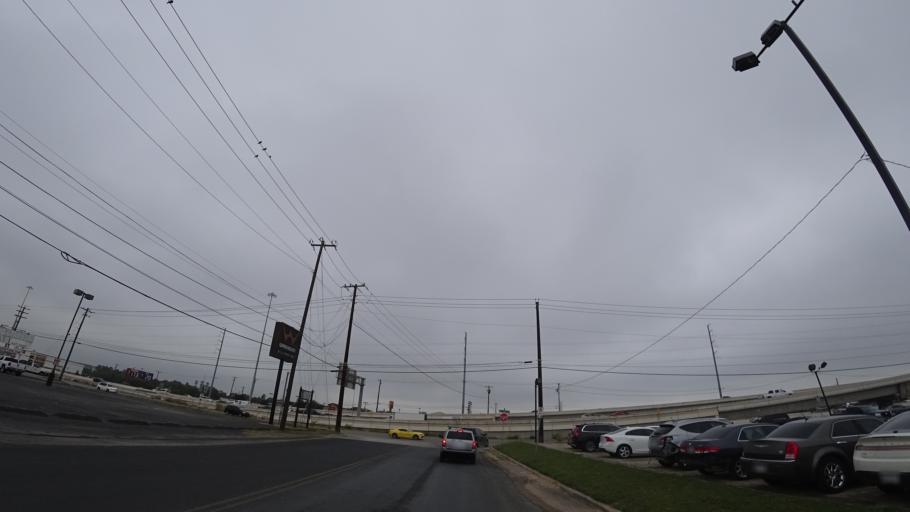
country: US
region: Texas
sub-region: Travis County
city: Austin
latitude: 30.2186
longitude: -97.7573
